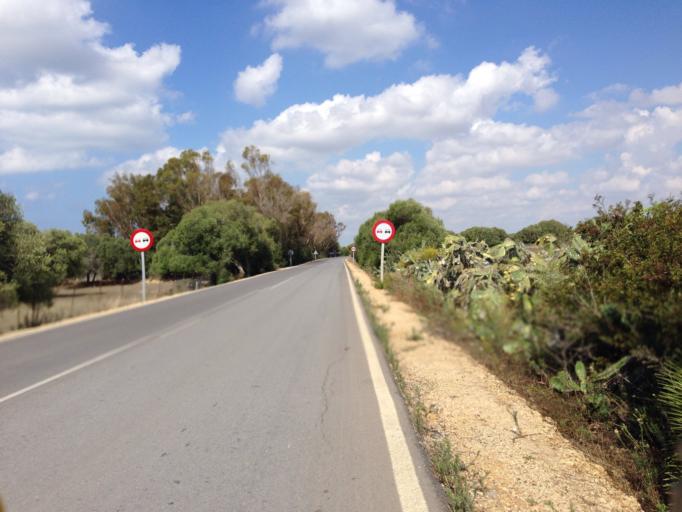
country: ES
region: Andalusia
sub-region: Provincia de Cadiz
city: Vejer de la Frontera
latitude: 36.2131
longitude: -6.0342
